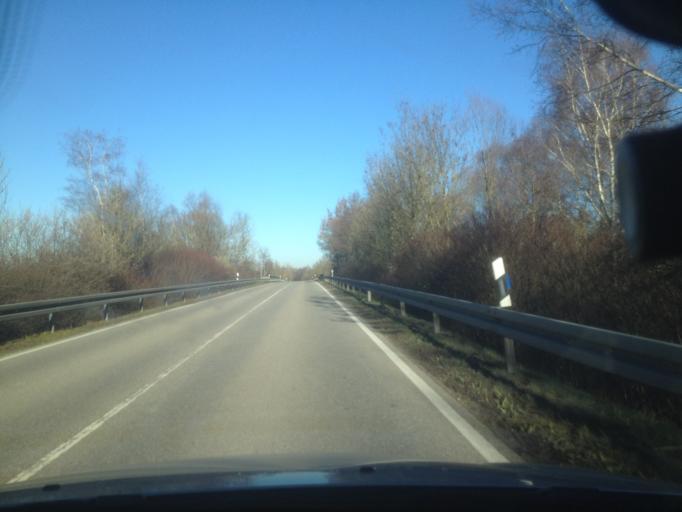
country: DE
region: Bavaria
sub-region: Upper Bavaria
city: Langenpreising
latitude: 48.4243
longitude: 11.9356
